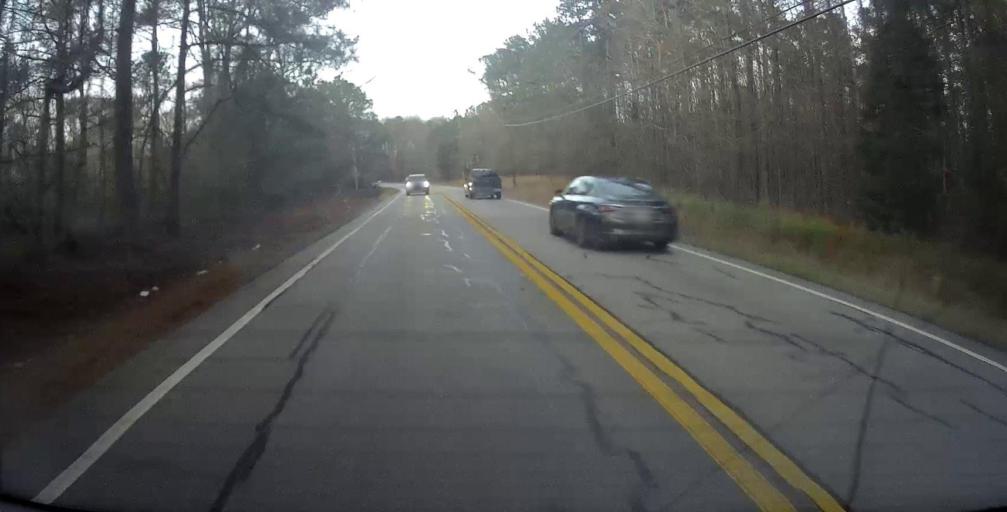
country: US
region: Alabama
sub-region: Russell County
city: Phenix City
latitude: 32.5799
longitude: -84.9114
